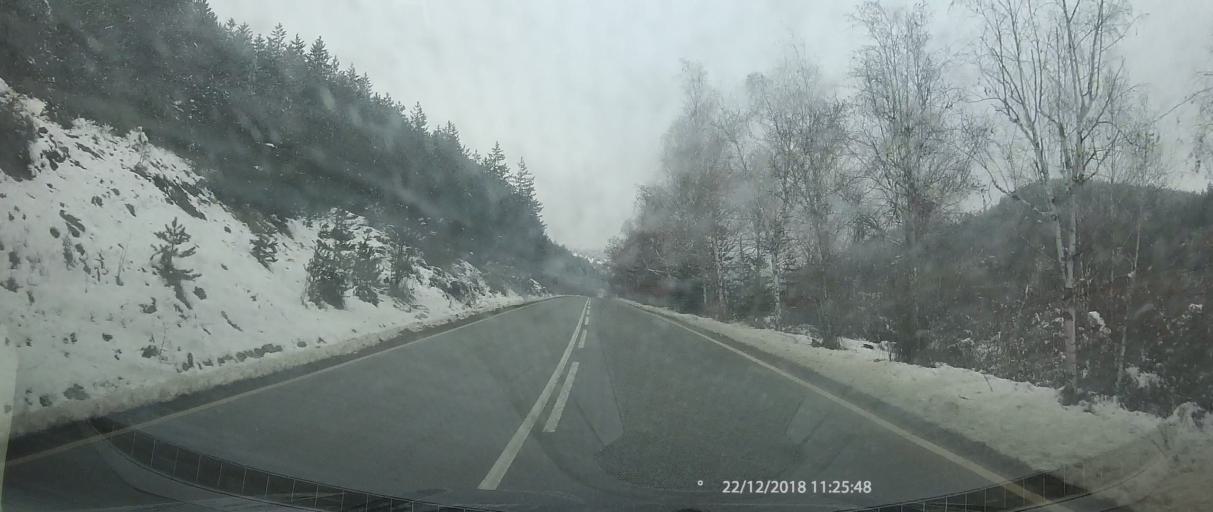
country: BG
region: Kyustendil
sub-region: Obshtina Boboshevo
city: Boboshevo
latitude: 42.2574
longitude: 22.9155
